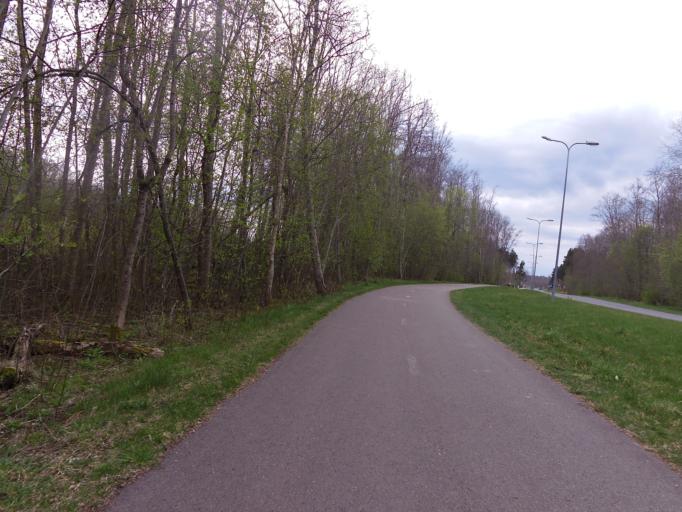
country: EE
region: Harju
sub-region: Kiili vald
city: Kiili
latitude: 59.3635
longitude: 24.8164
